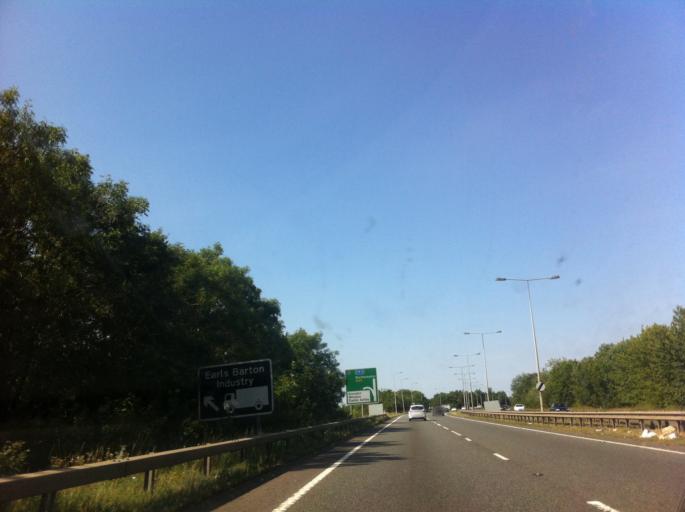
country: GB
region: England
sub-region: Northamptonshire
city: Earls Barton
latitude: 52.2591
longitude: -0.7365
